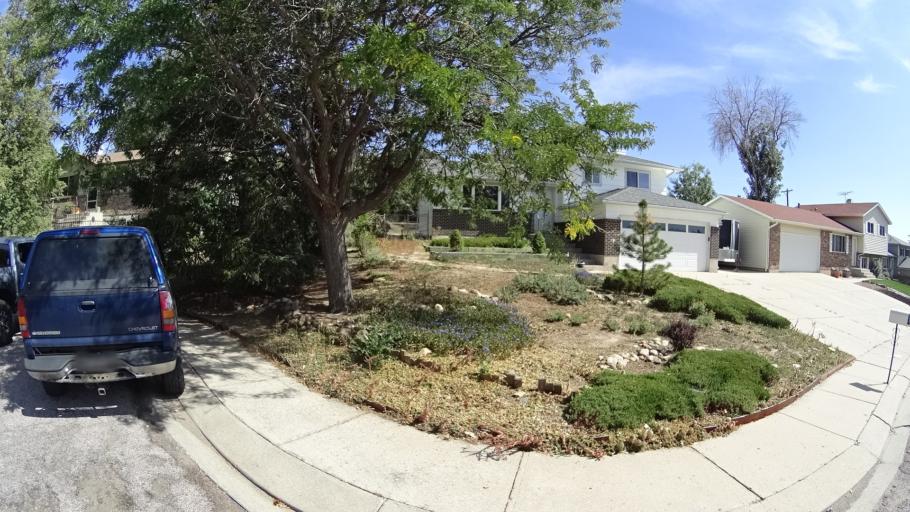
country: US
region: Colorado
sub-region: El Paso County
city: Cimarron Hills
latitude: 38.9026
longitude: -104.7526
